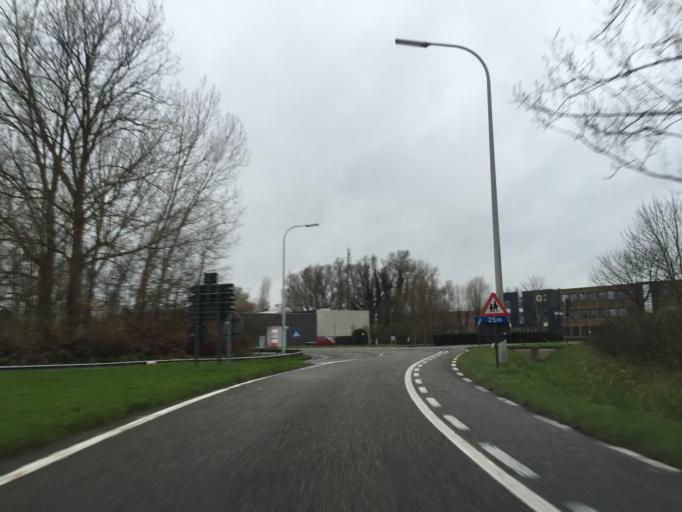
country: BE
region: Flanders
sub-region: Provincie Oost-Vlaanderen
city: Evergem
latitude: 51.0863
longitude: 3.6706
